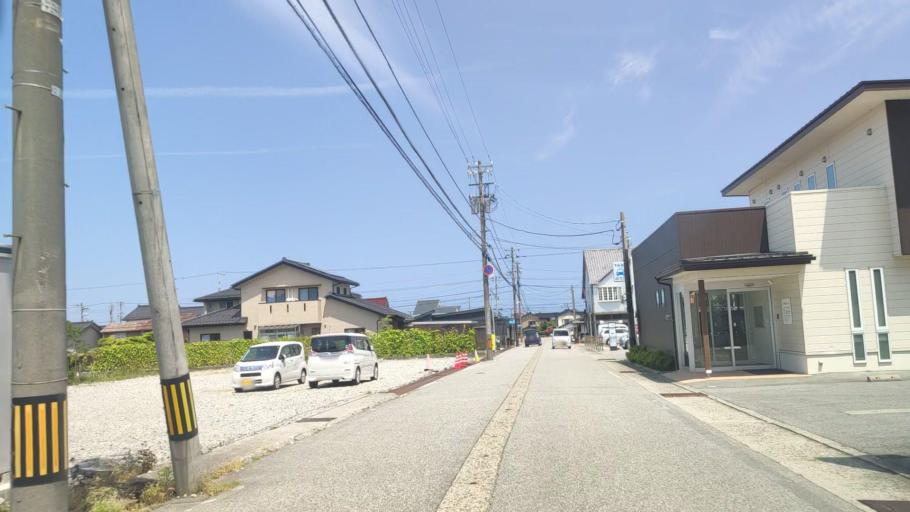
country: JP
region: Toyama
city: Nyuzen
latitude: 36.9571
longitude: 137.5593
